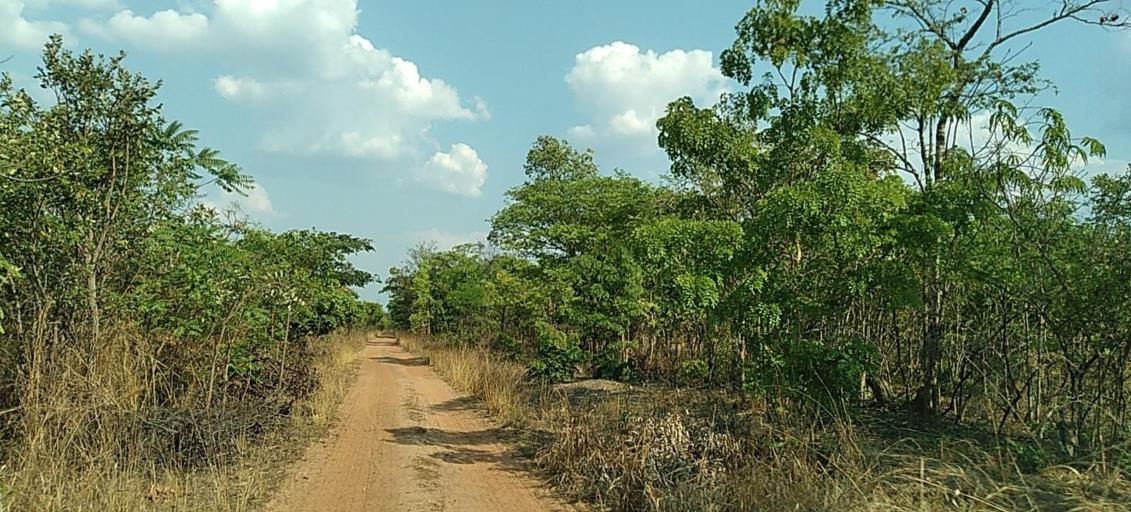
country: ZM
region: Copperbelt
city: Luanshya
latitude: -13.1631
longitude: 28.3421
